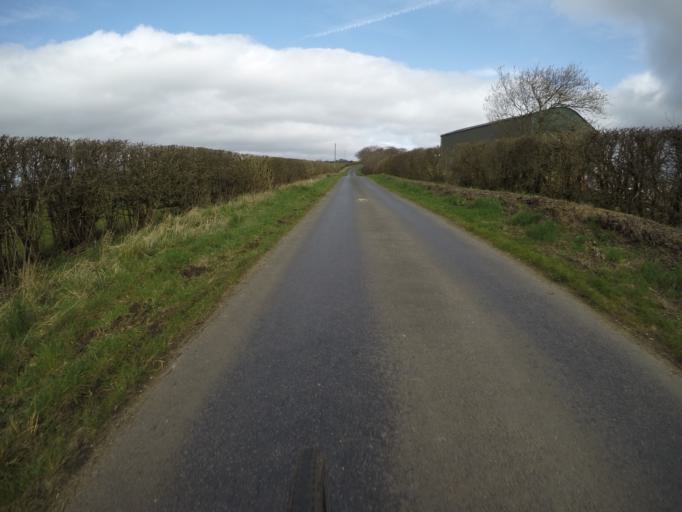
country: GB
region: Scotland
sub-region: North Ayrshire
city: Springside
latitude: 55.6558
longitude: -4.6100
